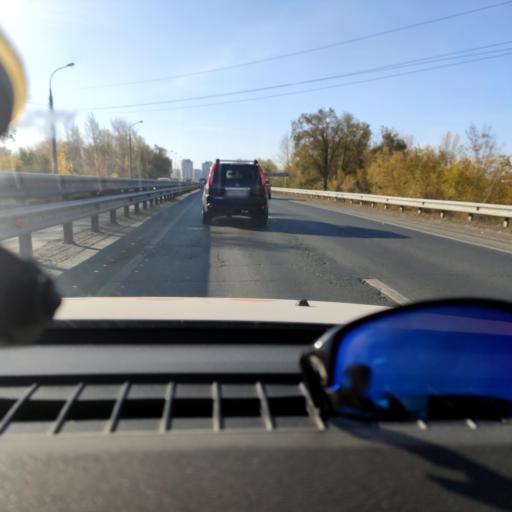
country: RU
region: Samara
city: Samara
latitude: 53.1058
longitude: 50.1632
